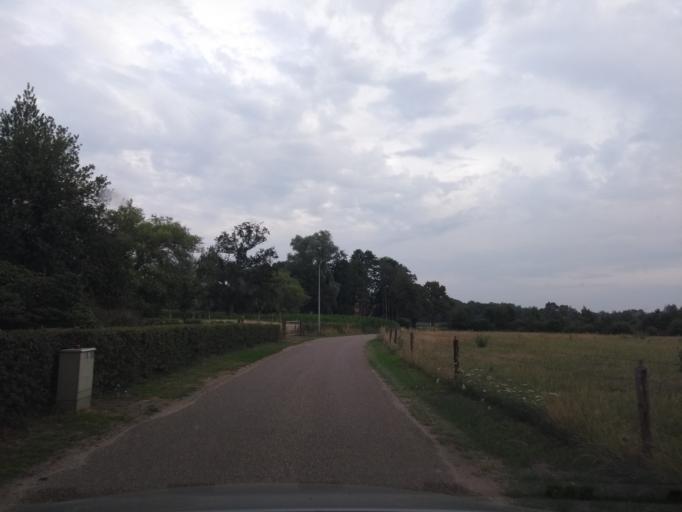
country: NL
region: Overijssel
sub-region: Gemeente Hengelo
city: Hengelo
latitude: 52.2313
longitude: 6.8258
